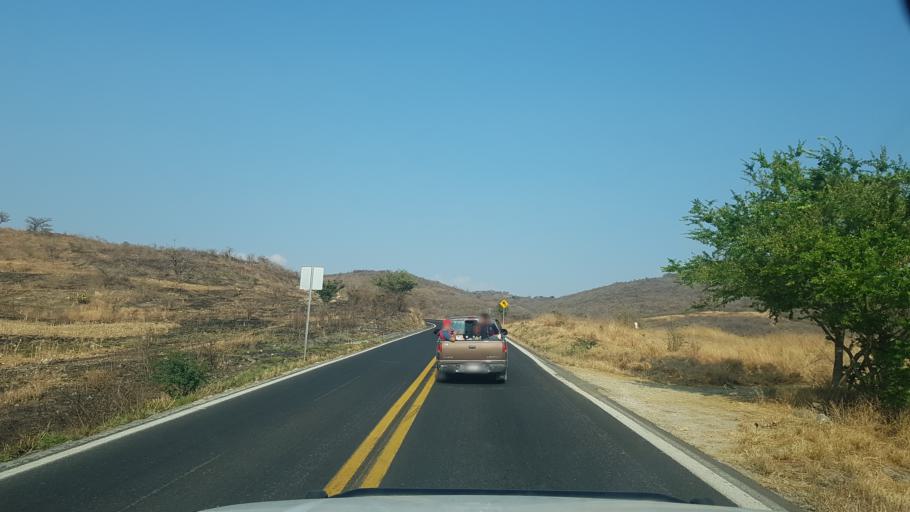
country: MX
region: Puebla
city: Calmeca
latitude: 18.6416
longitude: -98.6107
